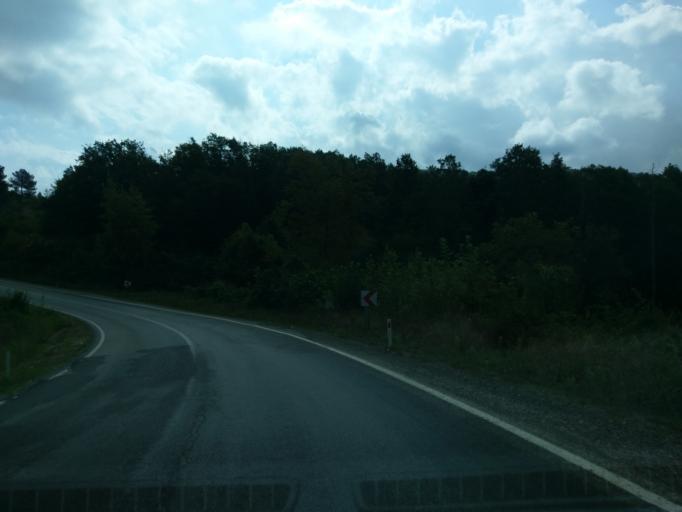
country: TR
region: Sinop
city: Yenikonak
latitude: 41.9450
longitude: 34.7576
